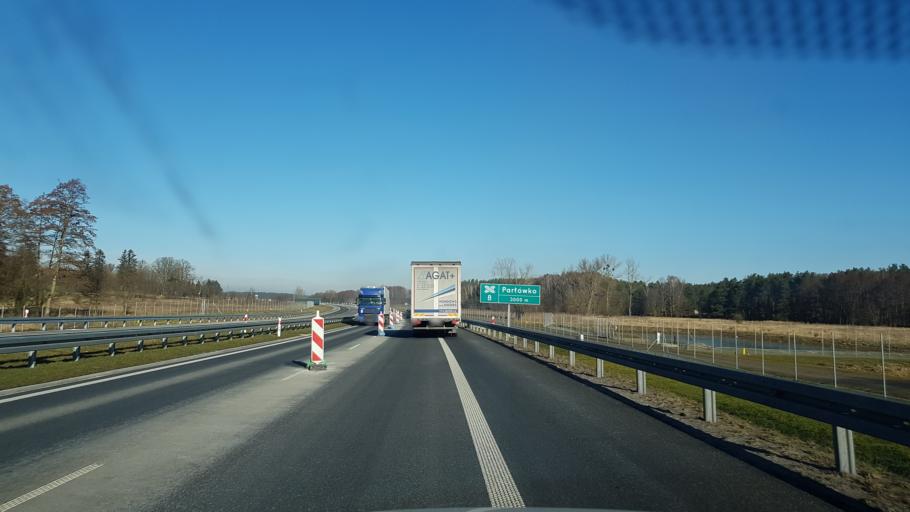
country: PL
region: West Pomeranian Voivodeship
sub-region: Powiat goleniowski
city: Przybiernow
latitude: 53.8077
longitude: 14.7715
